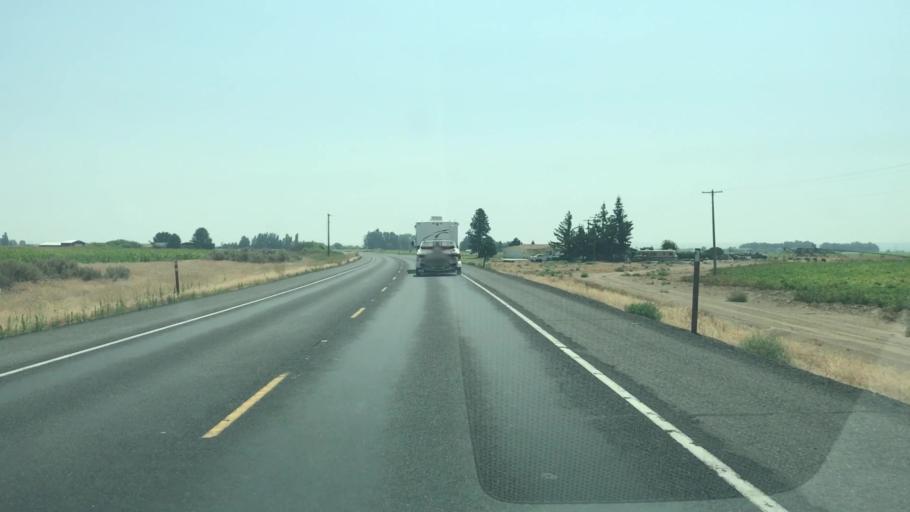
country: US
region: Washington
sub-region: Grant County
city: Quincy
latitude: 47.1132
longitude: -119.8493
